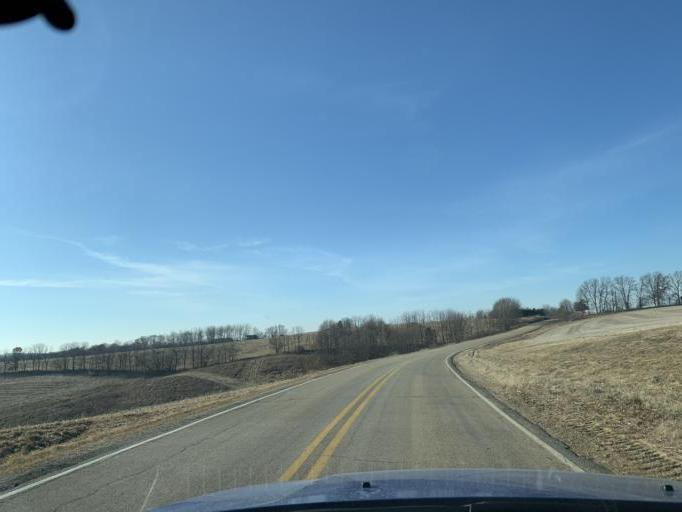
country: US
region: Wisconsin
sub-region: Iowa County
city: Barneveld
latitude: 42.8097
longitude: -89.8892
